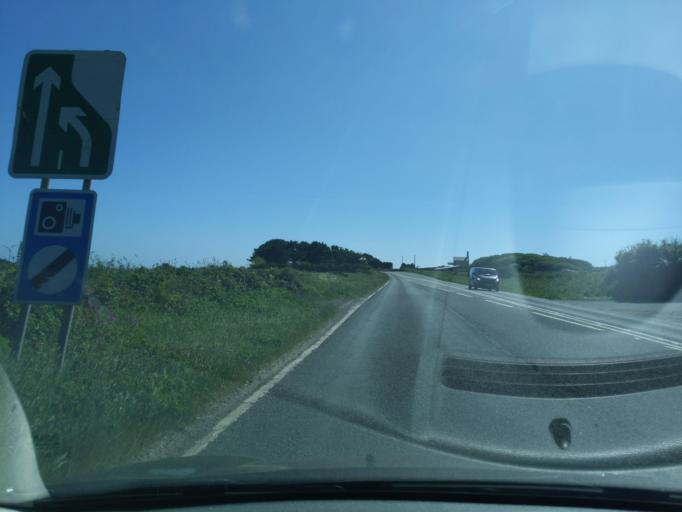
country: GB
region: England
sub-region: Cornwall
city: Wendron
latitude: 50.1415
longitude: -5.2163
